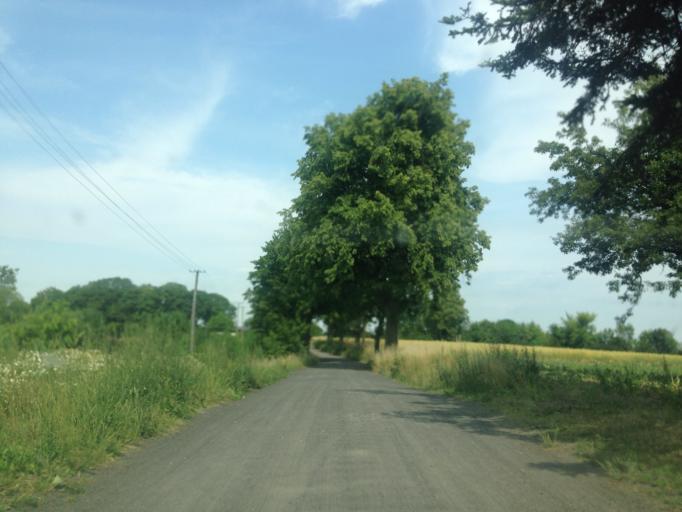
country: PL
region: Kujawsko-Pomorskie
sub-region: Powiat brodnicki
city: Bobrowo
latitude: 53.2739
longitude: 19.3133
